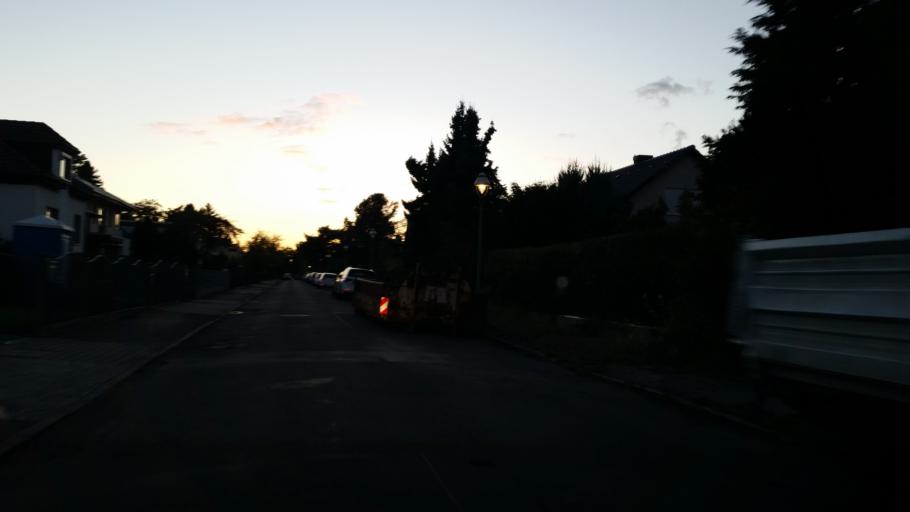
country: DE
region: Berlin
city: Lichtenrade
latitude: 52.4006
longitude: 13.4181
